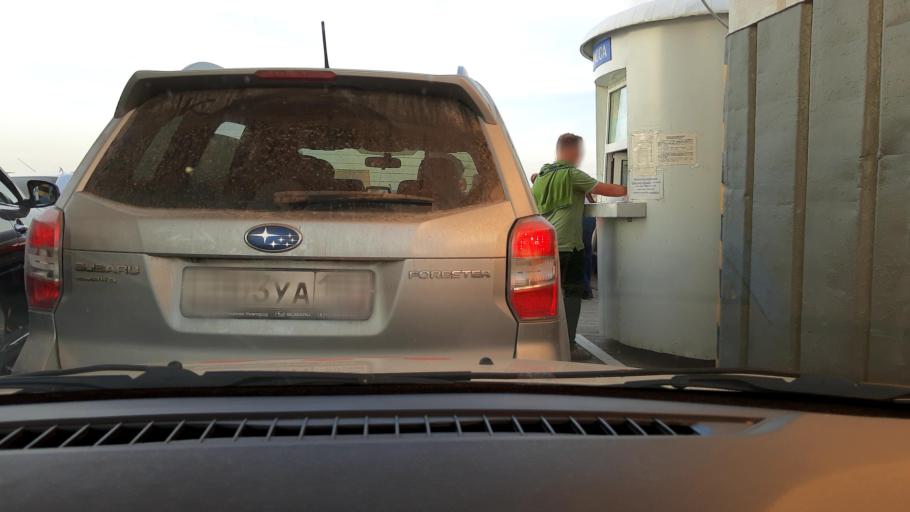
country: RU
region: Nizjnij Novgorod
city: Nizhniy Novgorod
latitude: 56.3351
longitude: 44.0261
